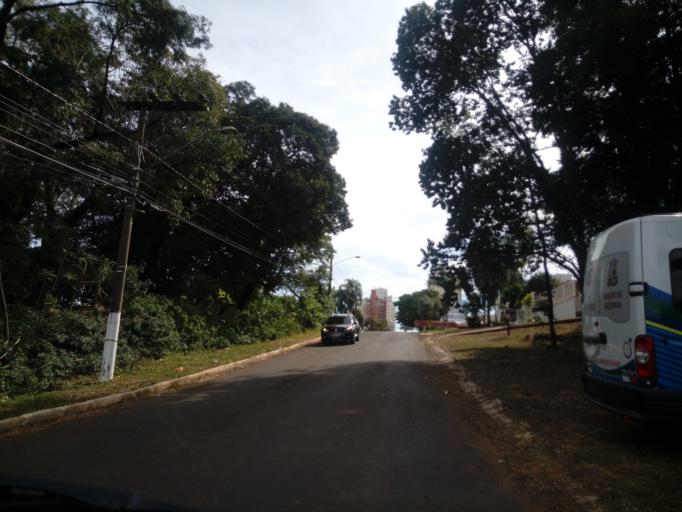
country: BR
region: Santa Catarina
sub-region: Chapeco
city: Chapeco
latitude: -27.1153
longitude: -52.6149
